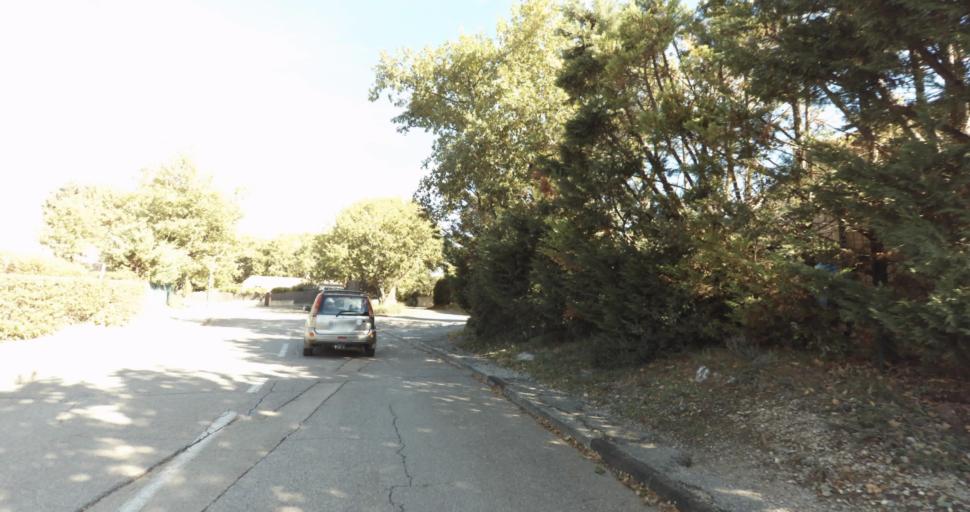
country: FR
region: Provence-Alpes-Cote d'Azur
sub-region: Departement des Bouches-du-Rhone
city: Venelles
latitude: 43.5934
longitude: 5.4725
